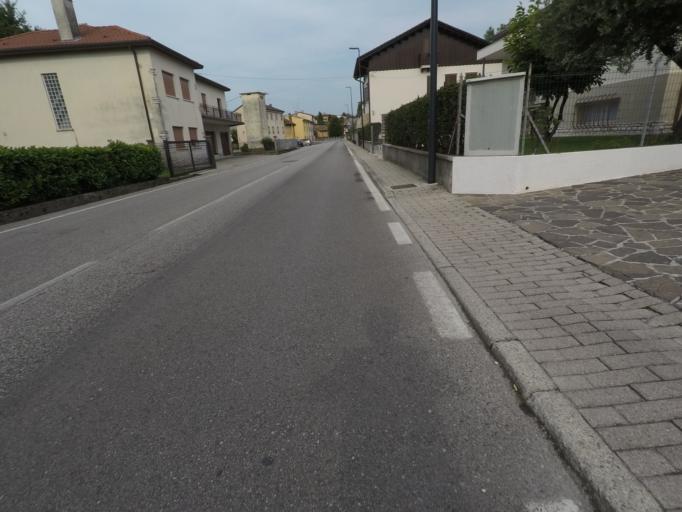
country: IT
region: Veneto
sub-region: Provincia di Treviso
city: Cappella Maggiore
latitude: 45.9698
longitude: 12.3596
